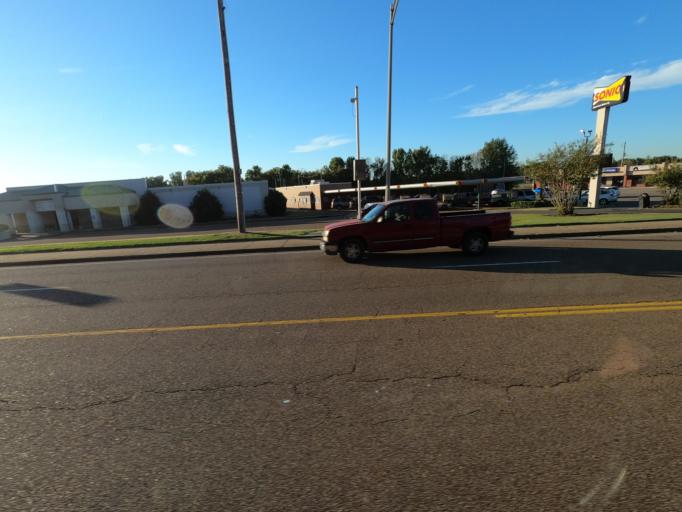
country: US
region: Tennessee
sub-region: Shelby County
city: Millington
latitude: 35.3473
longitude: -89.9038
